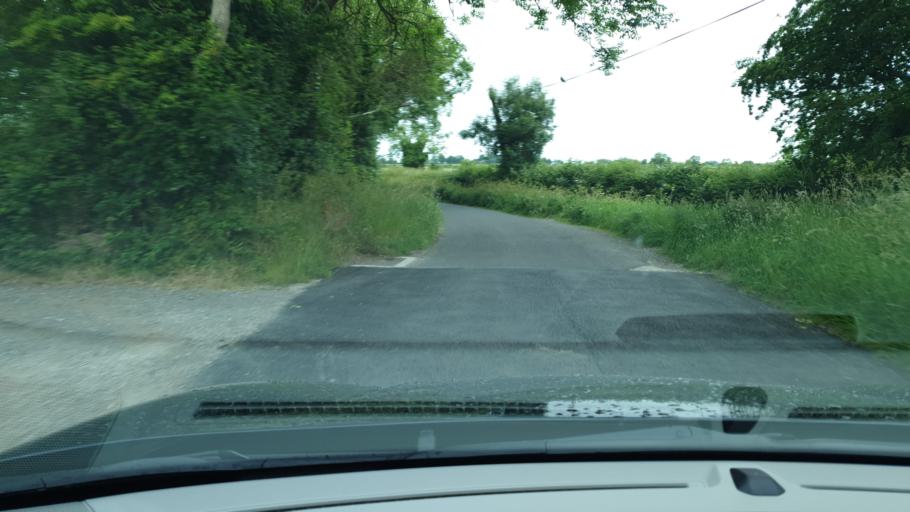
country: IE
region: Leinster
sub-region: An Mhi
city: Ashbourne
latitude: 53.5151
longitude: -6.3850
